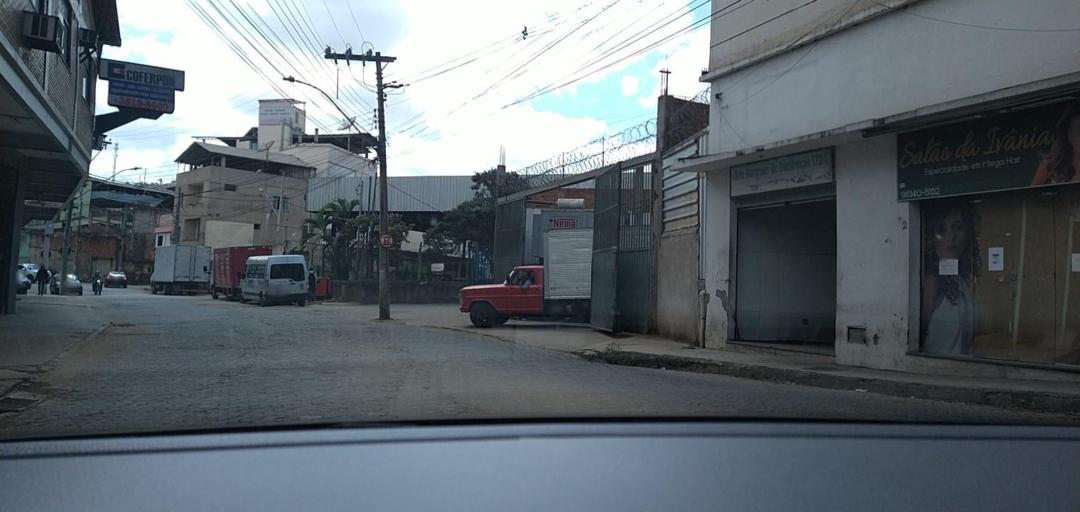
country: BR
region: Minas Gerais
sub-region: Ponte Nova
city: Ponte Nova
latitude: -20.4076
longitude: -42.8953
